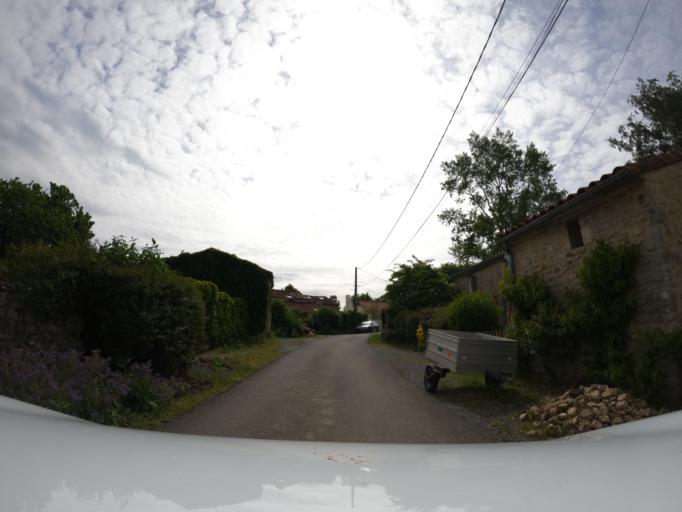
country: FR
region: Pays de la Loire
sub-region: Departement de la Vendee
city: Saint-Hilaire-des-Loges
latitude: 46.4898
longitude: -0.6616
